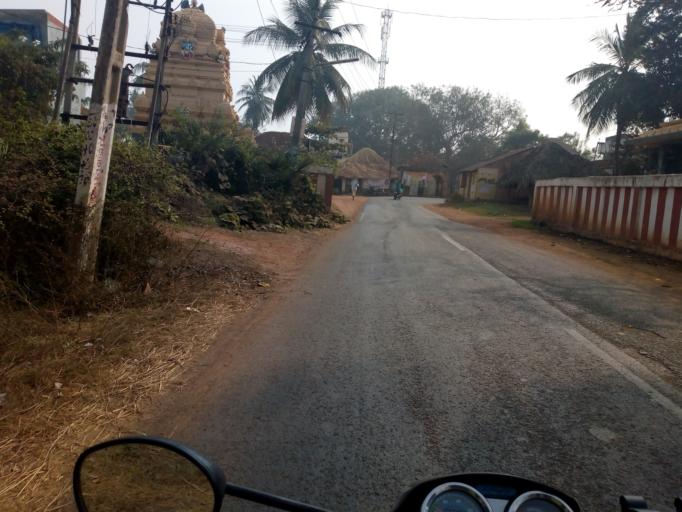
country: IN
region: Andhra Pradesh
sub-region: West Godavari
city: Tadepallegudem
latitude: 16.7761
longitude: 81.4254
